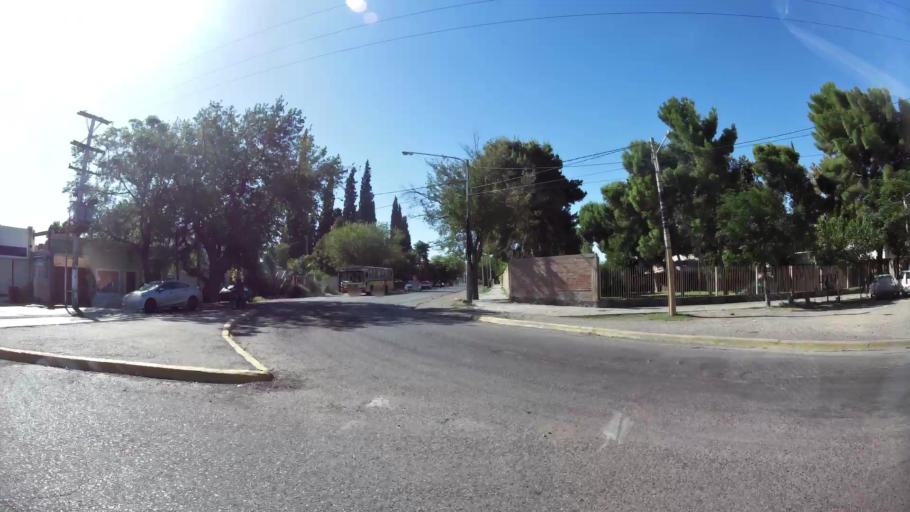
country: AR
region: San Juan
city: San Juan
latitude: -31.5197
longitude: -68.5368
